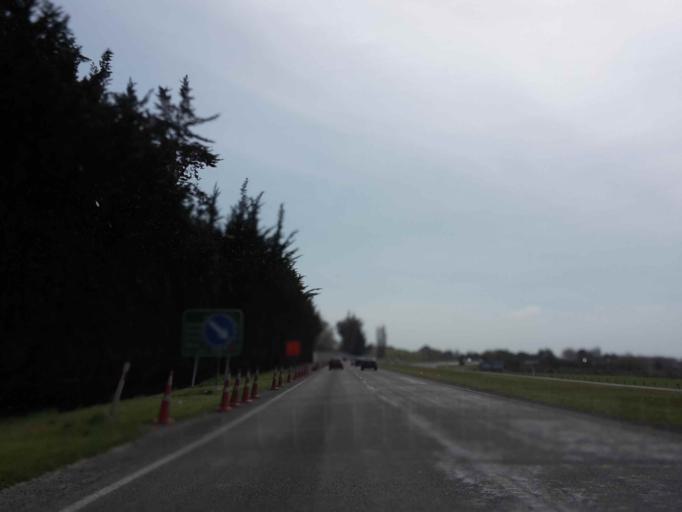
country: NZ
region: Canterbury
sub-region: Waimakariri District
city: Kaiapoi
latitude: -43.4351
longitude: 172.6386
